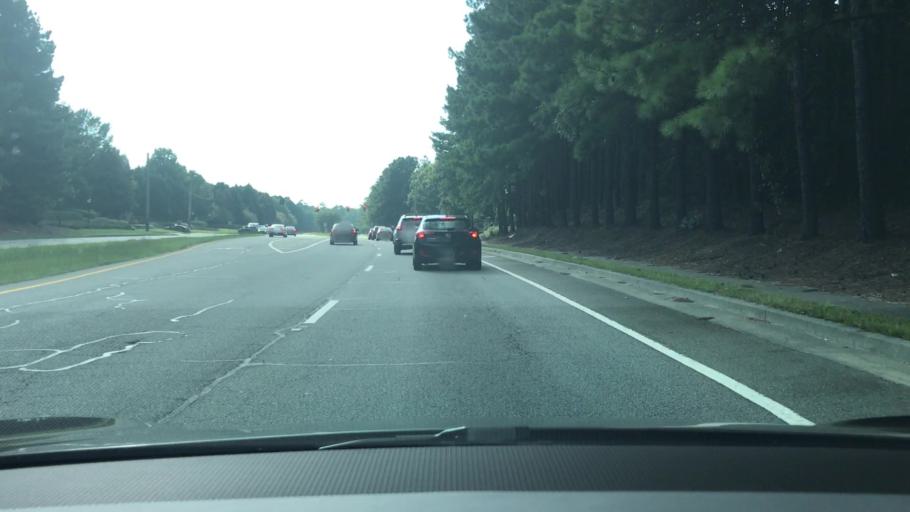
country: US
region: Georgia
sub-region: Gwinnett County
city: Duluth
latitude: 34.0101
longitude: -84.1020
